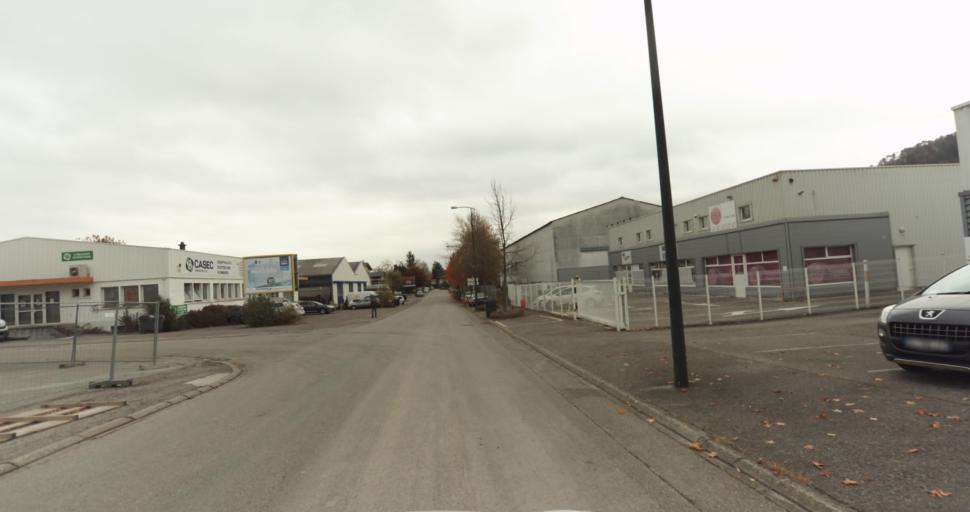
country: FR
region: Rhone-Alpes
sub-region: Departement de la Haute-Savoie
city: Annecy
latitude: 45.8868
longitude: 6.1140
